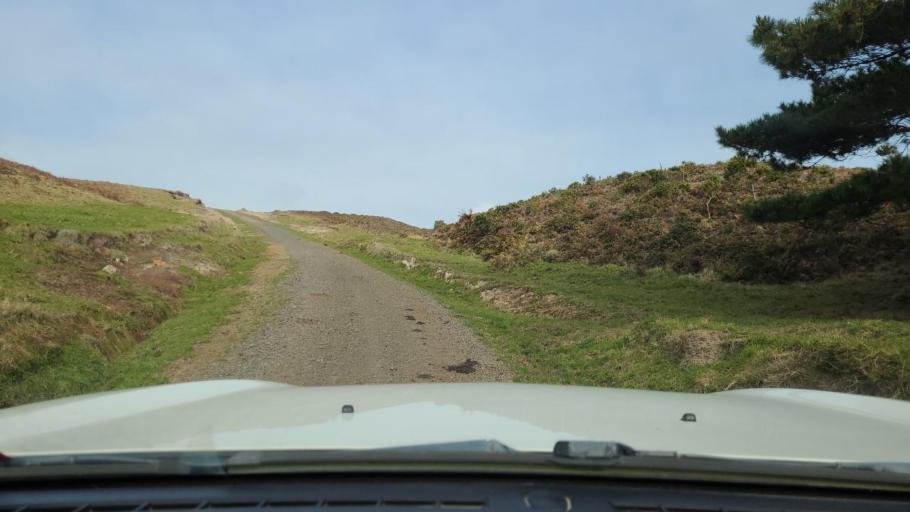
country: NZ
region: Chatham Islands
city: Waitangi
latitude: -44.0480
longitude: -176.6370
